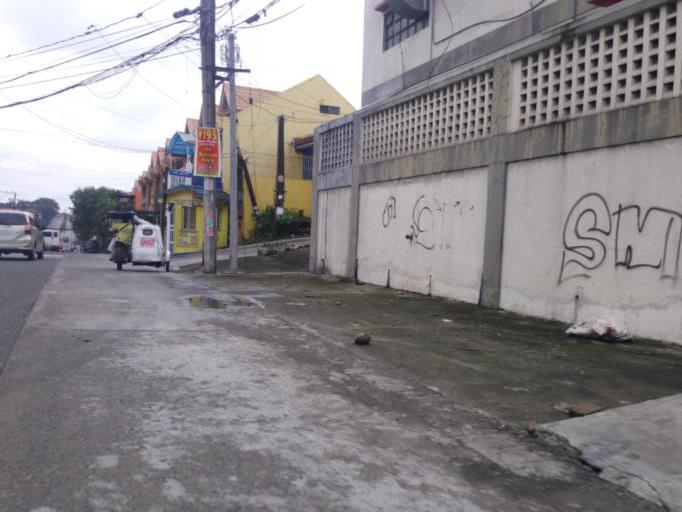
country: PH
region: Calabarzon
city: Bagong Pagasa
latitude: 14.7095
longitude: 121.0212
